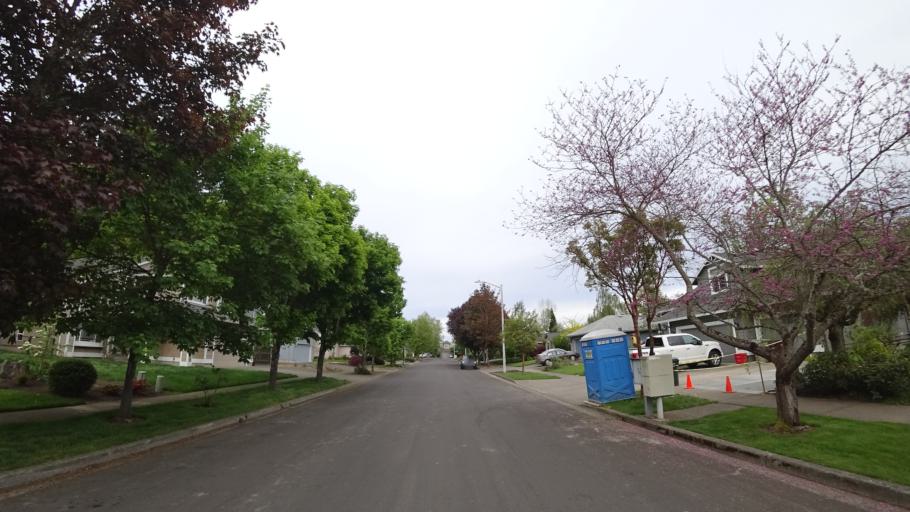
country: US
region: Oregon
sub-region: Washington County
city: Rockcreek
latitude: 45.5160
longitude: -122.9195
